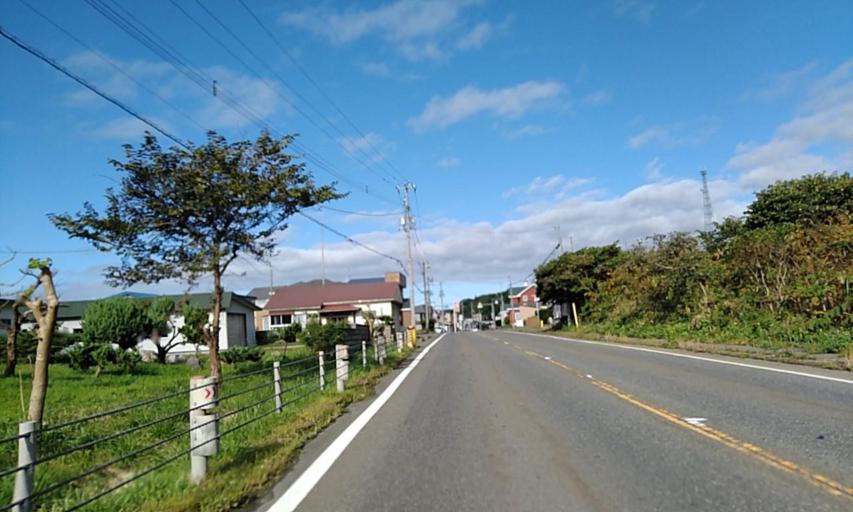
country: JP
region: Hokkaido
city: Shizunai-furukawacho
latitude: 42.2465
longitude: 142.5683
